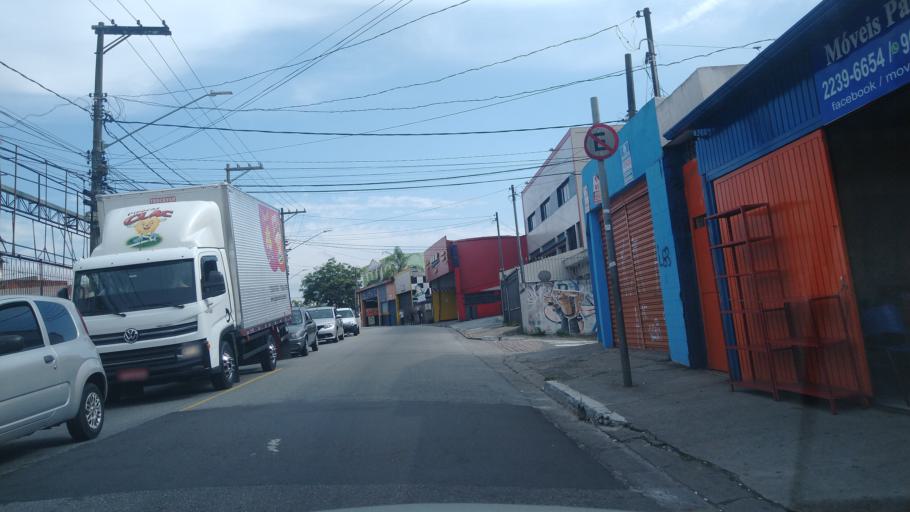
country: BR
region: Sao Paulo
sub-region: Sao Paulo
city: Sao Paulo
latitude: -23.4864
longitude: -46.6529
